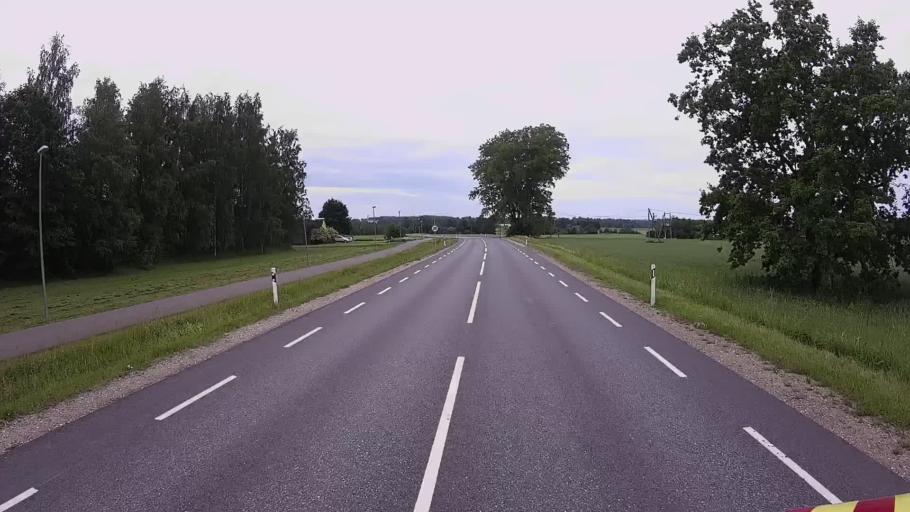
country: EE
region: Viljandimaa
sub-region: Karksi vald
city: Karksi-Nuia
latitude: 58.1182
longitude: 25.5796
